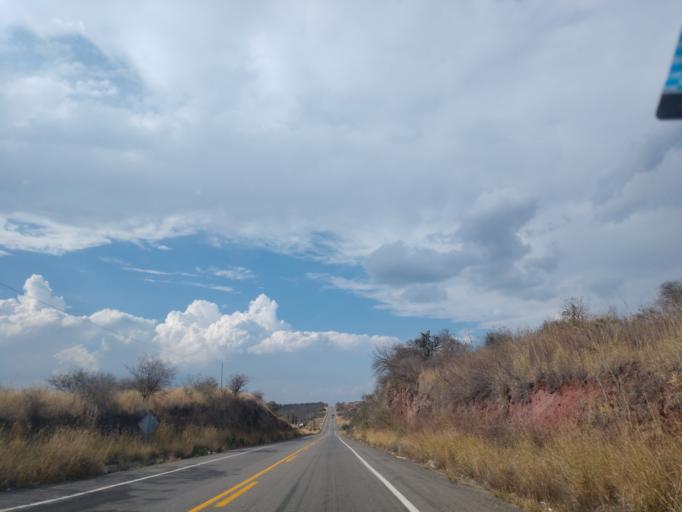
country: MX
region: Jalisco
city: La Manzanilla de la Paz
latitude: 20.0850
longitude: -103.1657
